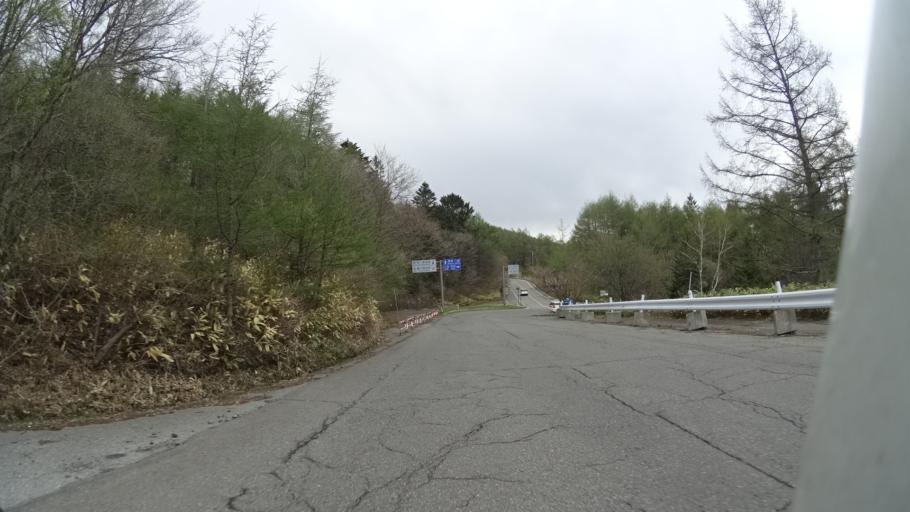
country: JP
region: Nagano
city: Suwa
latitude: 36.1503
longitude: 138.1449
